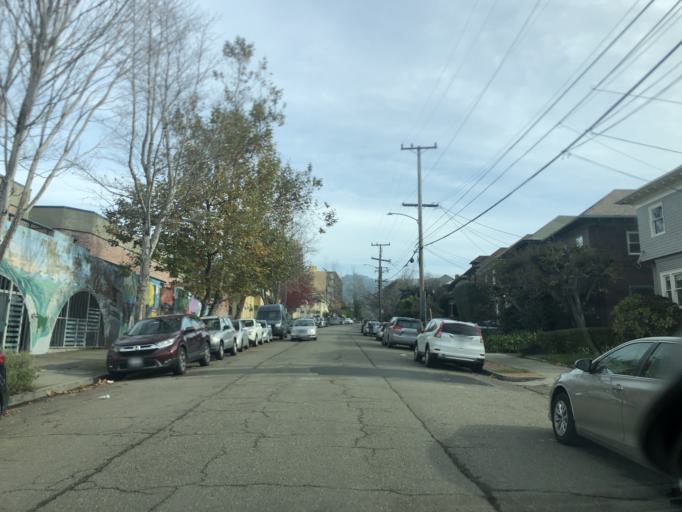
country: US
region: California
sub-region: Alameda County
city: Berkeley
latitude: 37.8596
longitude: -122.2588
